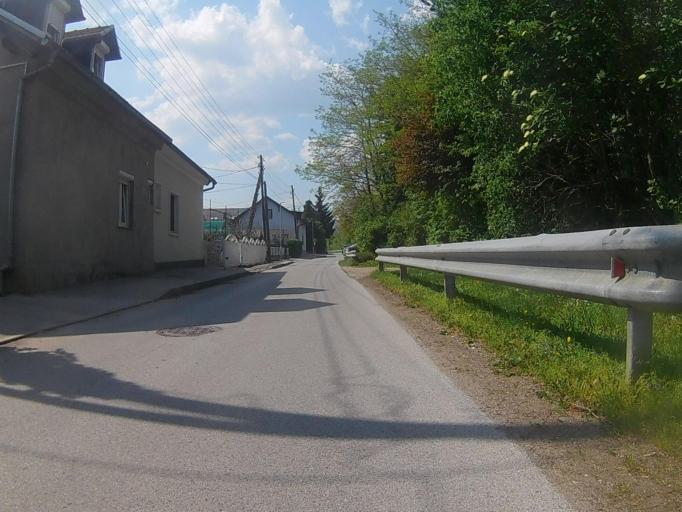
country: SI
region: Maribor
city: Kamnica
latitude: 46.5609
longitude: 15.6194
